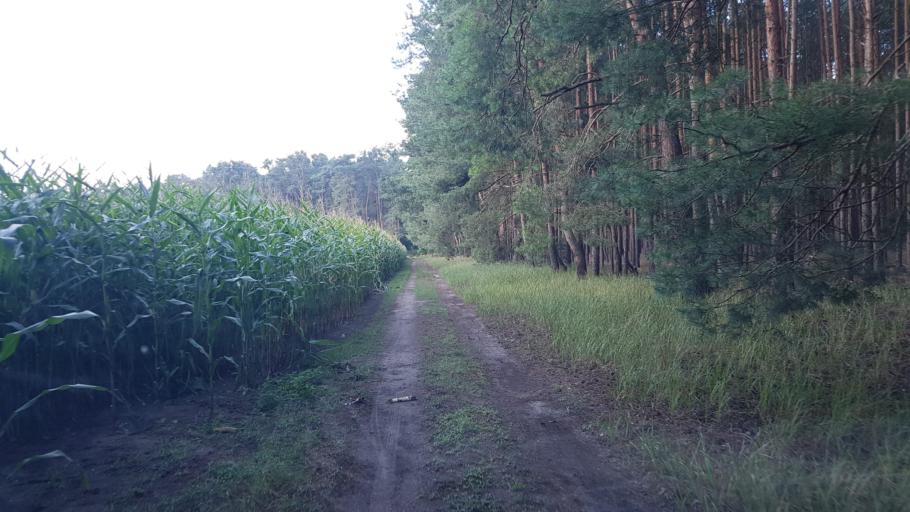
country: DE
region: Brandenburg
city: Schonewalde
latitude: 51.7049
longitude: 13.5816
